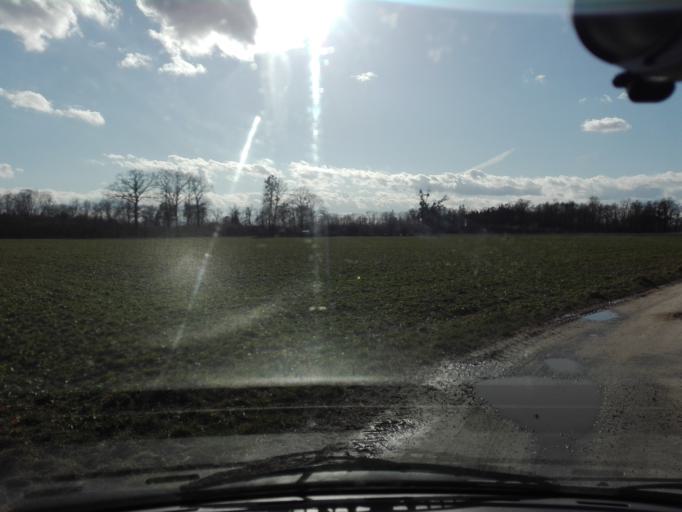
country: AT
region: Upper Austria
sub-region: Politischer Bezirk Perg
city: Perg
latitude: 48.2227
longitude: 14.6572
